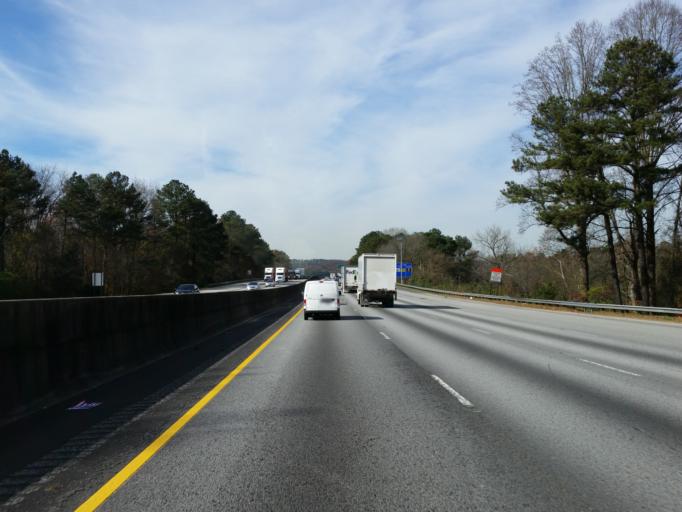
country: US
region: Georgia
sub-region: Cobb County
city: Mableton
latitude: 33.7681
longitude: -84.5329
